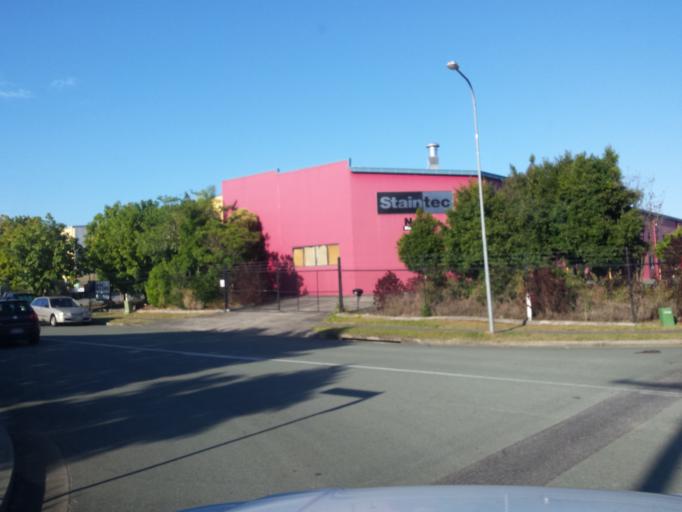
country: AU
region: Queensland
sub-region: Logan
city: Slacks Creek
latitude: -27.6631
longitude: 153.1357
